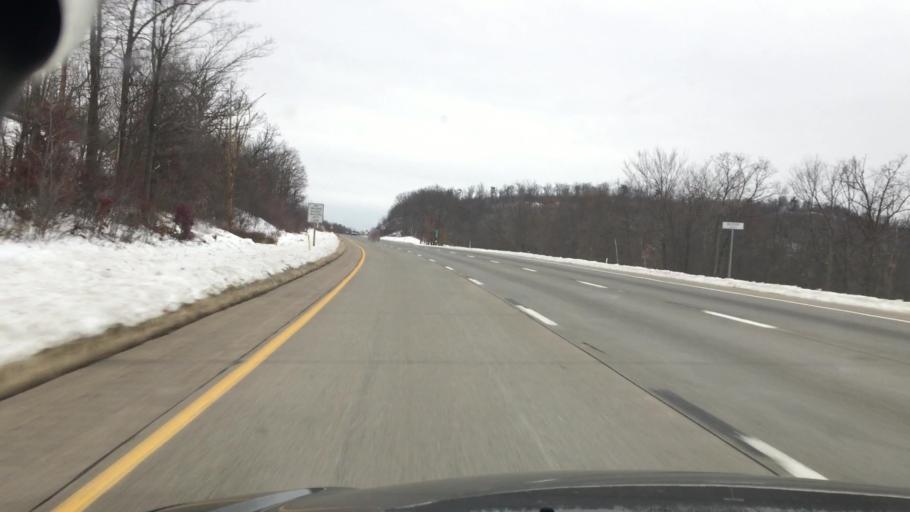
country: US
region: Pennsylvania
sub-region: Luzerne County
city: Harleigh
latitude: 41.0687
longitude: -75.9856
